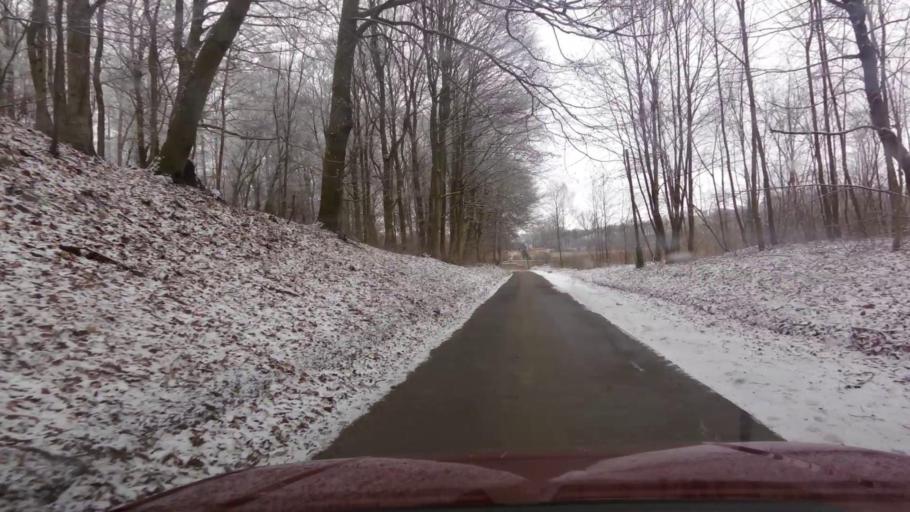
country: PL
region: West Pomeranian Voivodeship
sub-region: Powiat swidwinski
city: Polczyn-Zdroj
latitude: 53.7858
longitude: 16.0431
